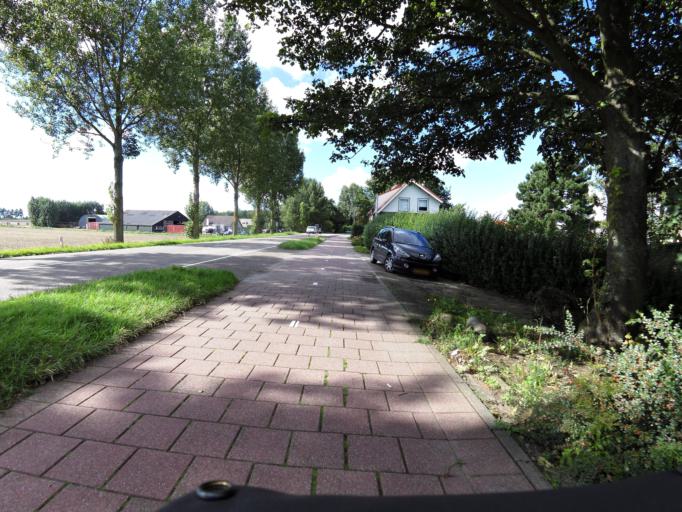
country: NL
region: South Holland
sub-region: Gemeente Goeree-Overflakkee
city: Middelharnis
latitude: 51.7301
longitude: 4.2380
